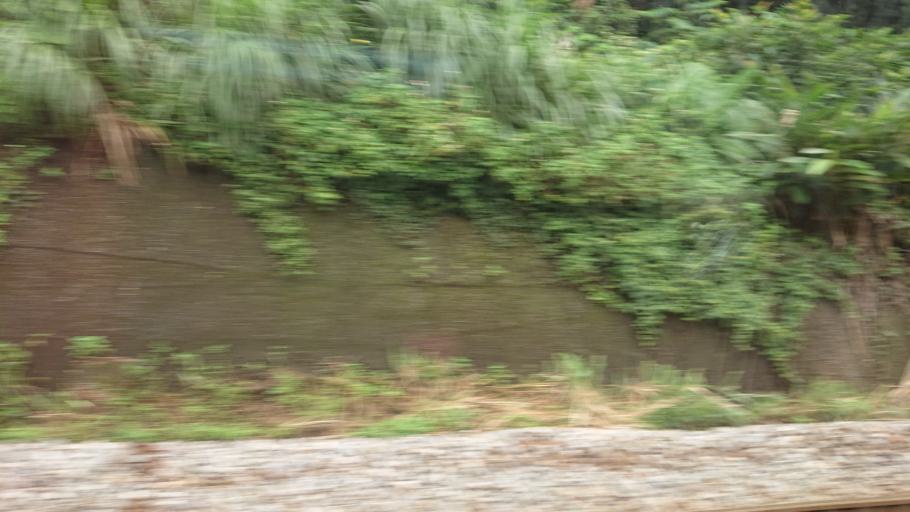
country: TW
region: Taiwan
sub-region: Keelung
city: Keelung
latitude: 25.0995
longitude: 121.8324
